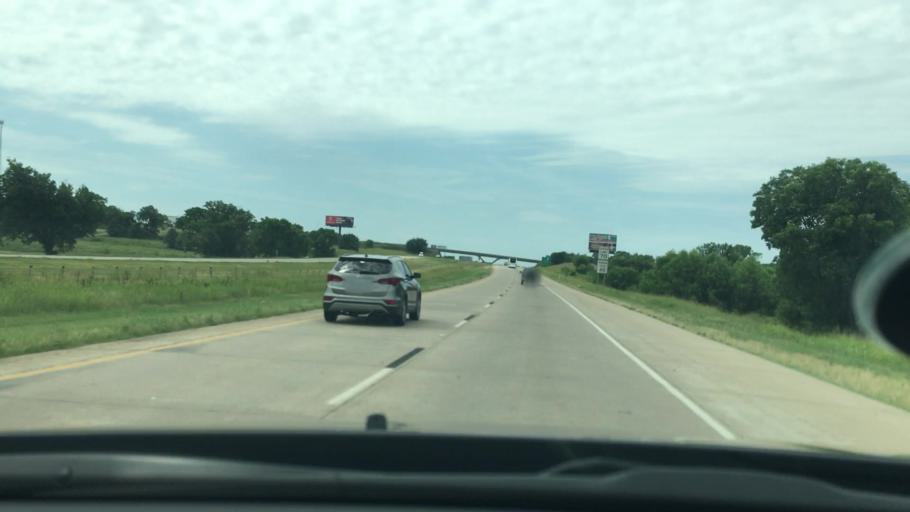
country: US
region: Oklahoma
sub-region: Carter County
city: Ardmore
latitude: 34.3240
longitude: -97.1557
